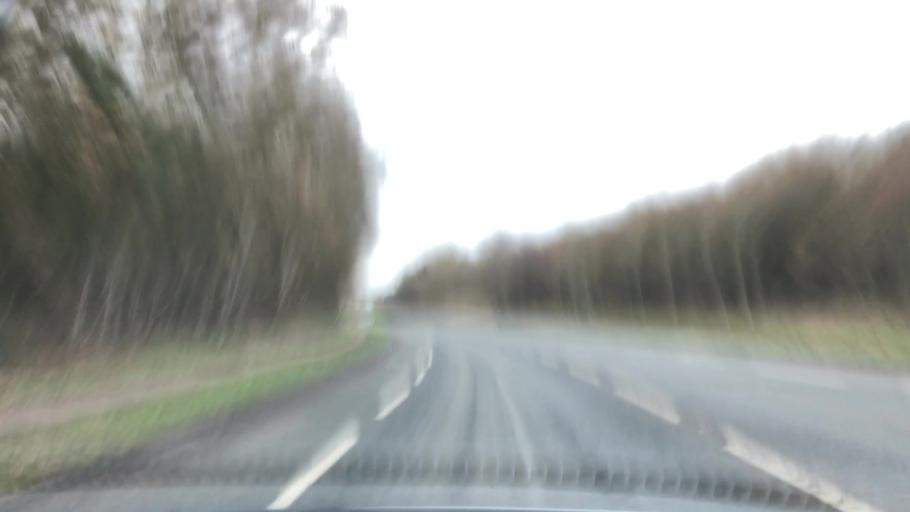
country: GB
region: England
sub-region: Coventry
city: Keresley
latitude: 52.4271
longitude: -1.5506
